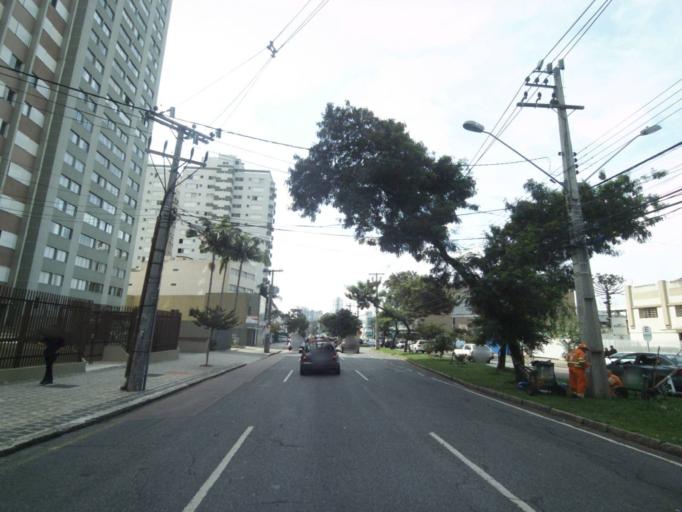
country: BR
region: Parana
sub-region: Curitiba
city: Curitiba
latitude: -25.4385
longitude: -49.2644
